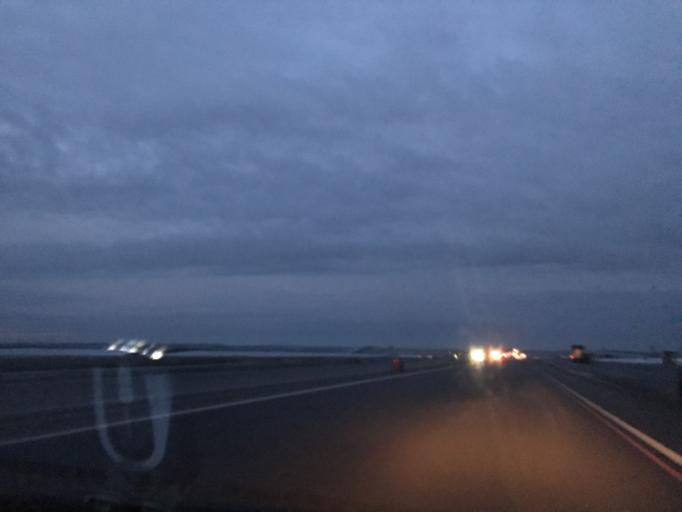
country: RU
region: Rostov
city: Samarskoye
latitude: 47.0161
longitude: 39.7348
